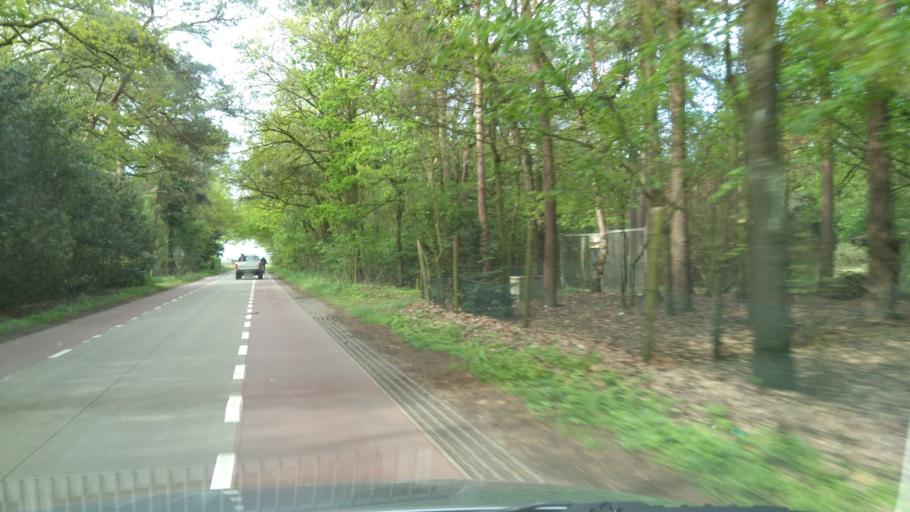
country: NL
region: North Brabant
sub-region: Gemeente Baarle-Nassau
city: Baarle-Nassau
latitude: 51.4330
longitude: 4.9113
